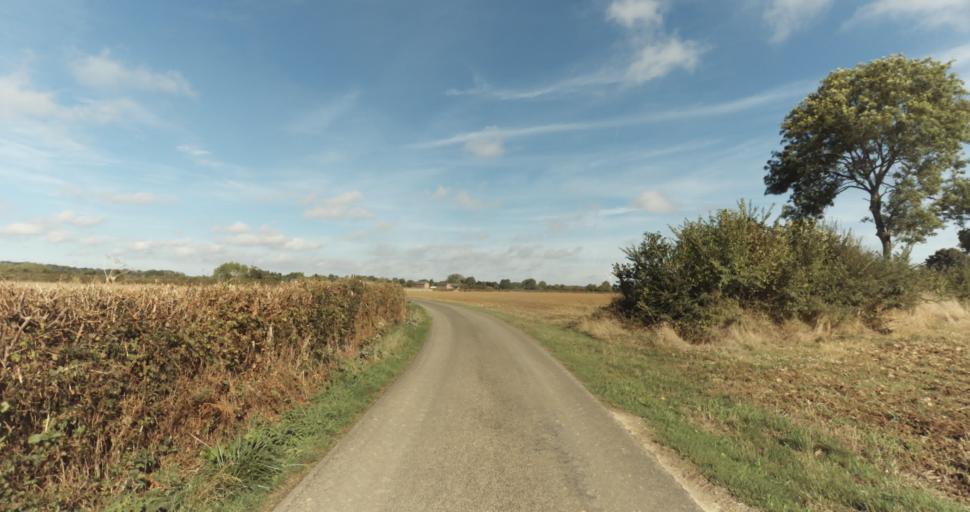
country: FR
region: Lower Normandy
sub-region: Departement du Calvados
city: Orbec
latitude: 48.9291
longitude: 0.3488
